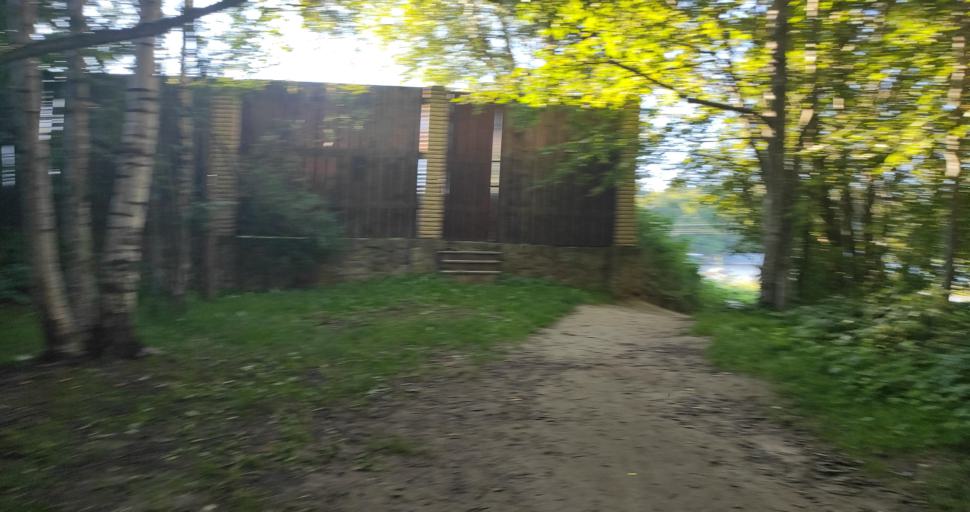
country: RU
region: Leningrad
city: Toksovo
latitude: 60.1544
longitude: 30.5558
